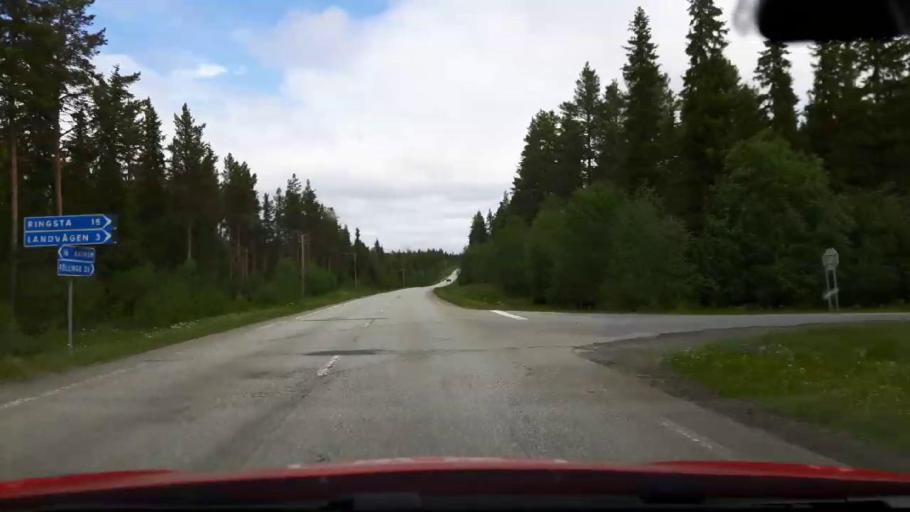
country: SE
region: Jaemtland
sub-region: Krokoms Kommun
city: Krokom
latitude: 63.4588
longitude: 14.4911
